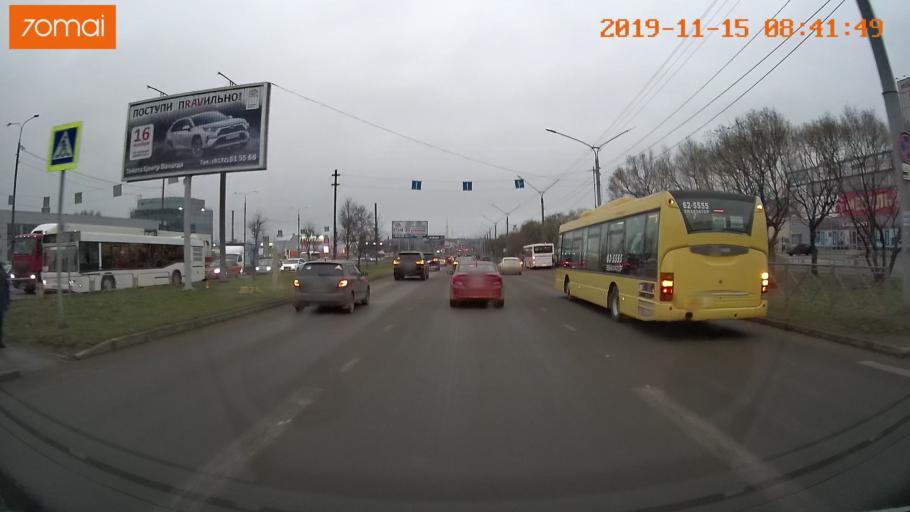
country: RU
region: Vologda
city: Cherepovets
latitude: 59.0985
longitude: 37.9113
